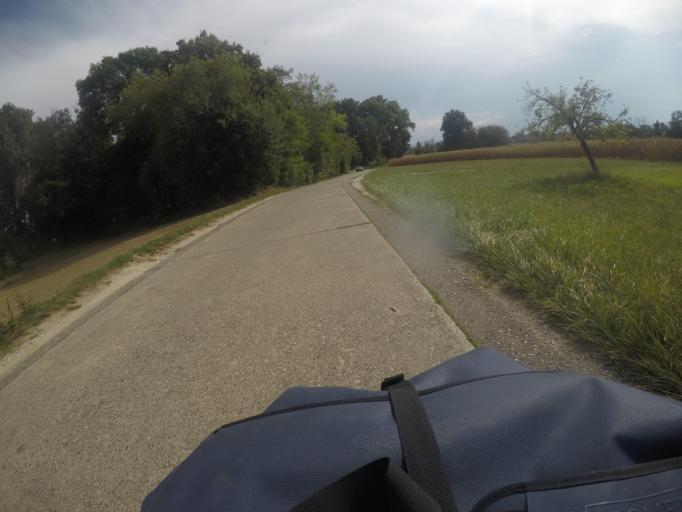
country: DE
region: Baden-Wuerttemberg
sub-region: Freiburg Region
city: Efringen-Kirchen
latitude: 47.6427
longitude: 7.5666
